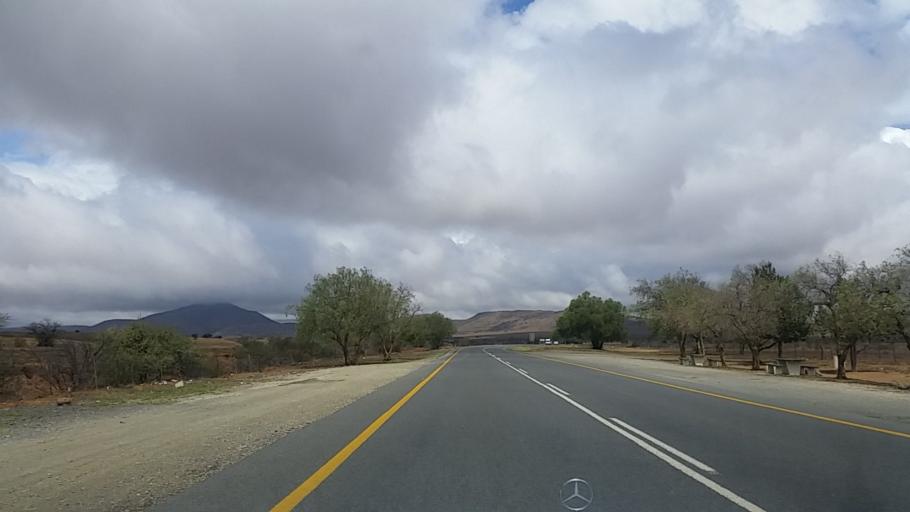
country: ZA
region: Eastern Cape
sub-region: Cacadu District Municipality
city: Graaff-Reinet
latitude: -32.0691
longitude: 24.6057
